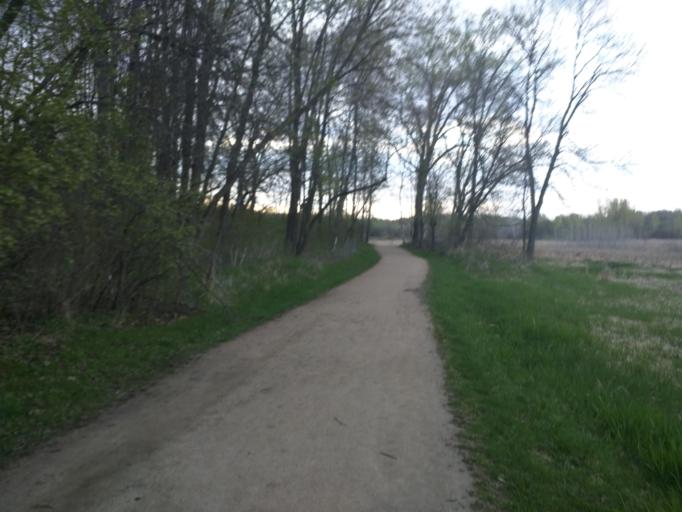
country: US
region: Minnesota
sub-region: Hennepin County
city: Minnetonka
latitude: 44.8990
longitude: -93.5009
